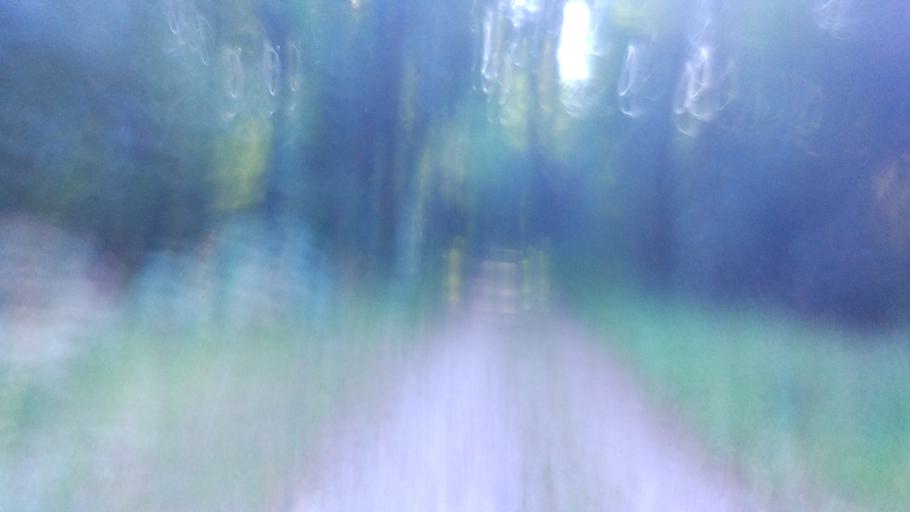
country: FR
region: Alsace
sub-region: Departement du Bas-Rhin
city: Gries
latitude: 48.7601
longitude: 7.8344
